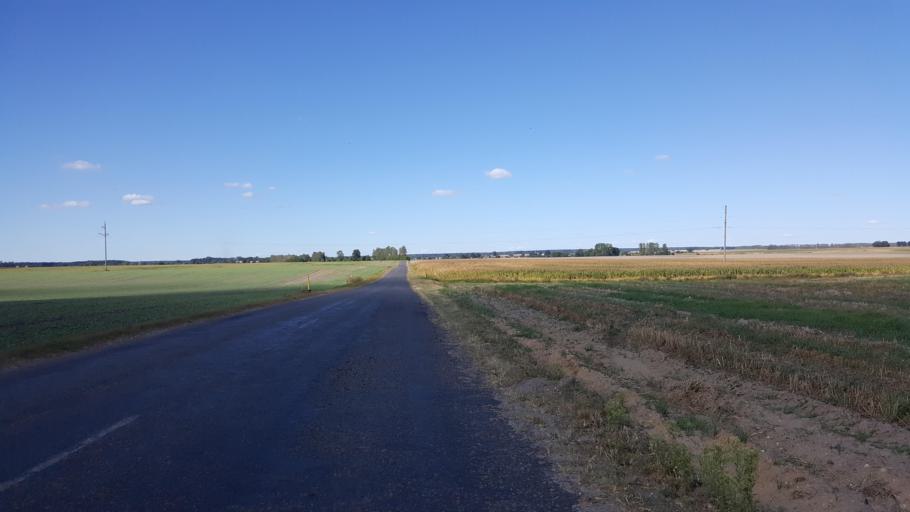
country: BY
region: Brest
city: Vysokaye
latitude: 52.2788
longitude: 23.4858
